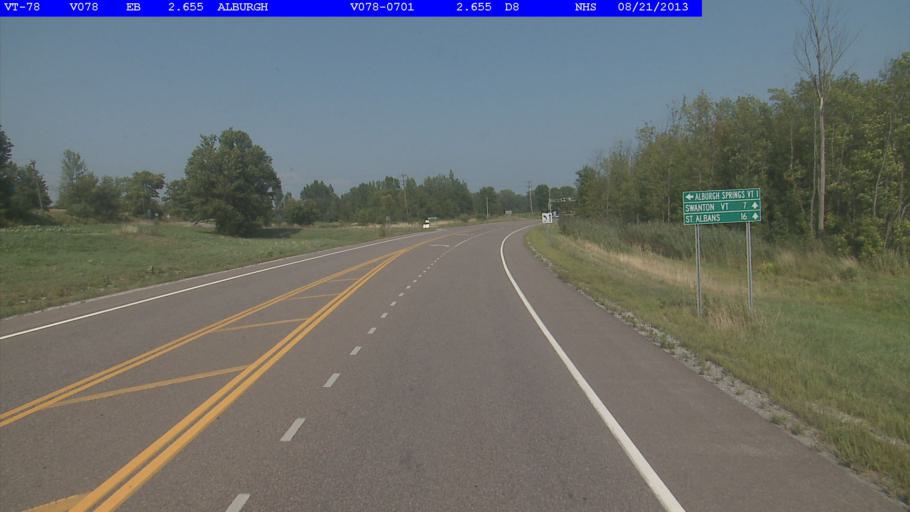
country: US
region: Vermont
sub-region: Franklin County
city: Swanton
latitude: 44.9742
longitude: -73.2328
